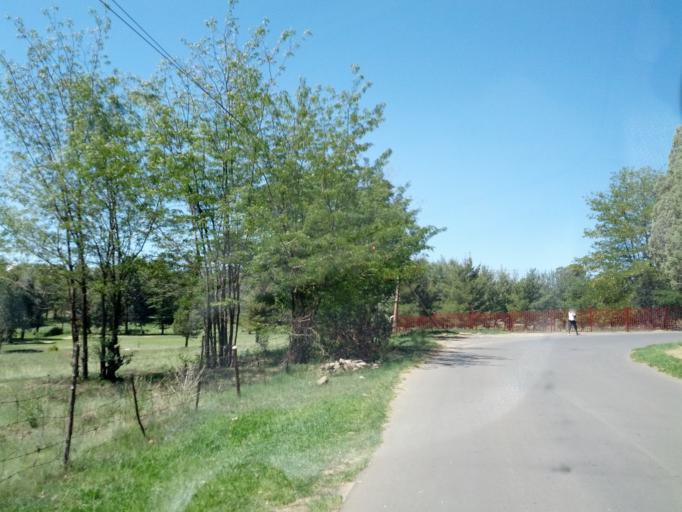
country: LS
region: Maseru
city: Maseru
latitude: -29.3110
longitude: 27.4725
